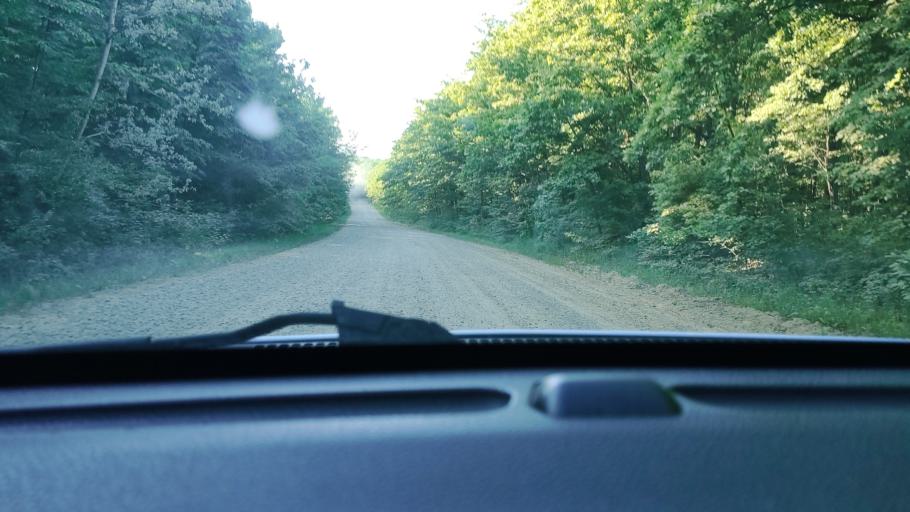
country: RU
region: Krasnodarskiy
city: Goryachiy Klyuch
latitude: 44.7100
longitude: 38.9924
